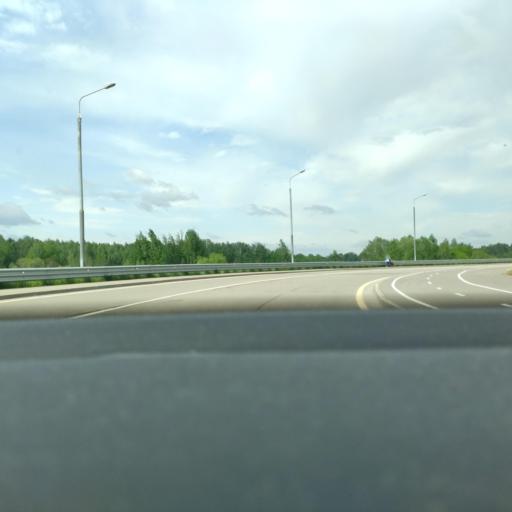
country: RU
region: Moscow
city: Severnyy
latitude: 55.9322
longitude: 37.5389
